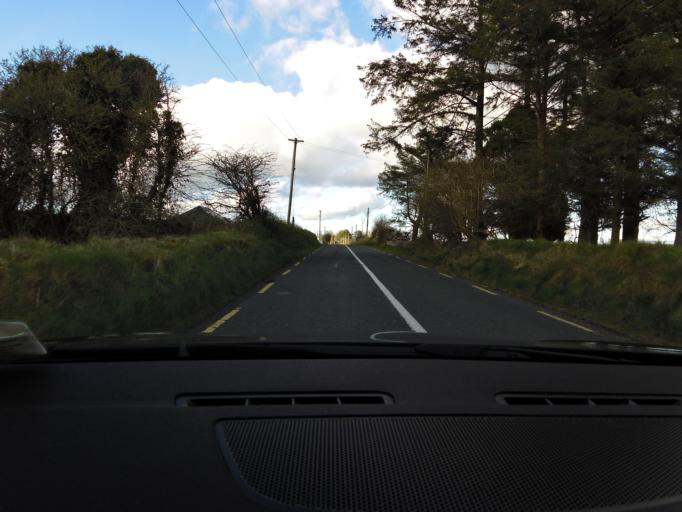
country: IE
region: Connaught
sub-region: Roscommon
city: Castlerea
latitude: 53.6692
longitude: -8.4995
